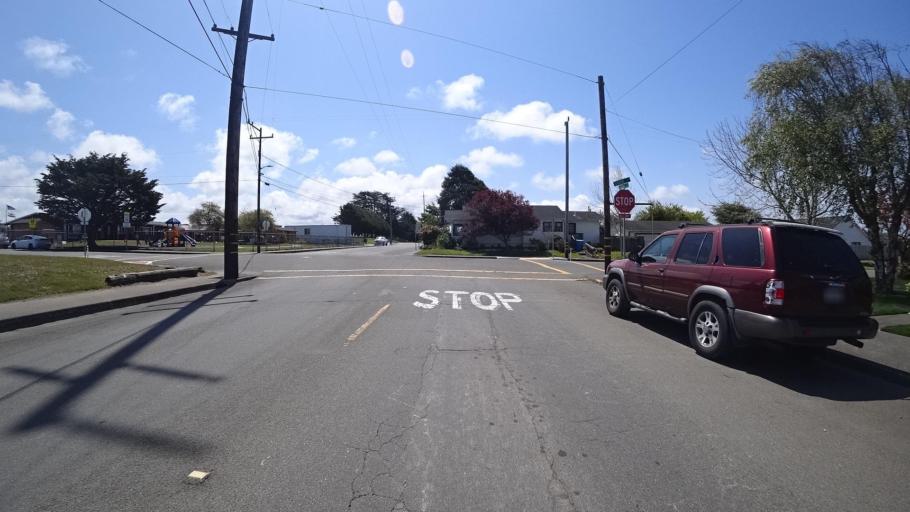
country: US
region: California
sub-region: Humboldt County
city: Bayview
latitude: 40.7778
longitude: -124.1803
